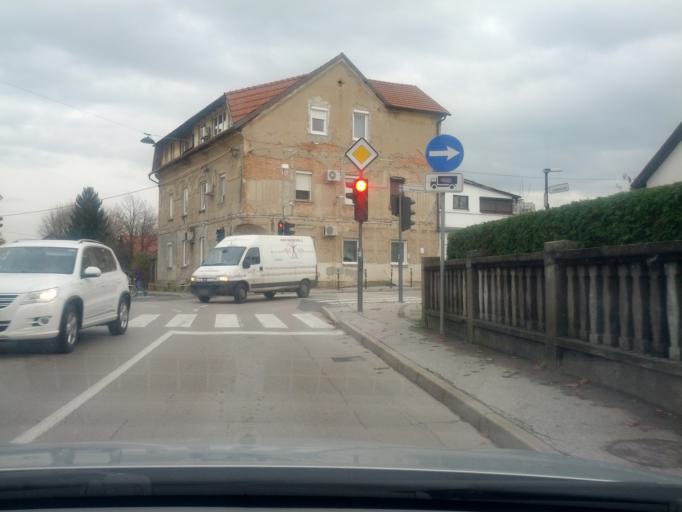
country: SI
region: Ljubljana
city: Ljubljana
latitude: 46.0448
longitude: 14.4796
